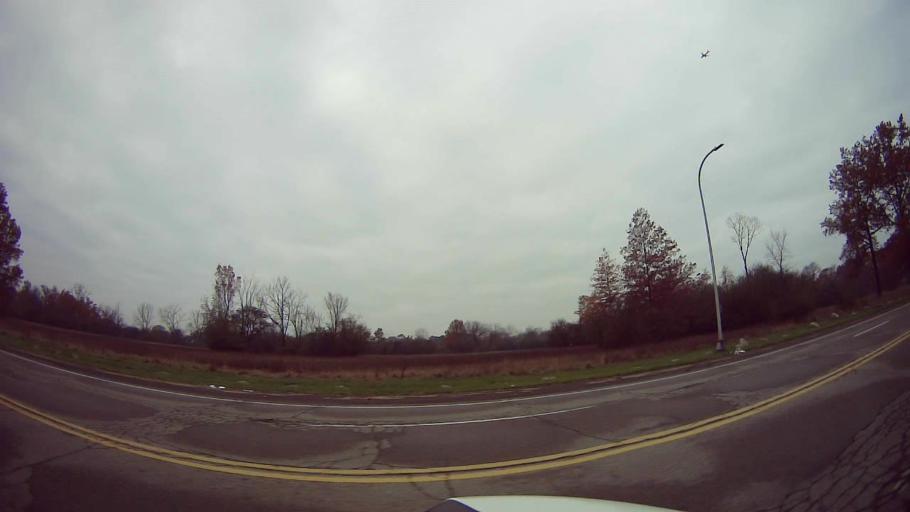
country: US
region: Michigan
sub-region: Wayne County
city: Dearborn Heights
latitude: 42.3476
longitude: -83.2505
